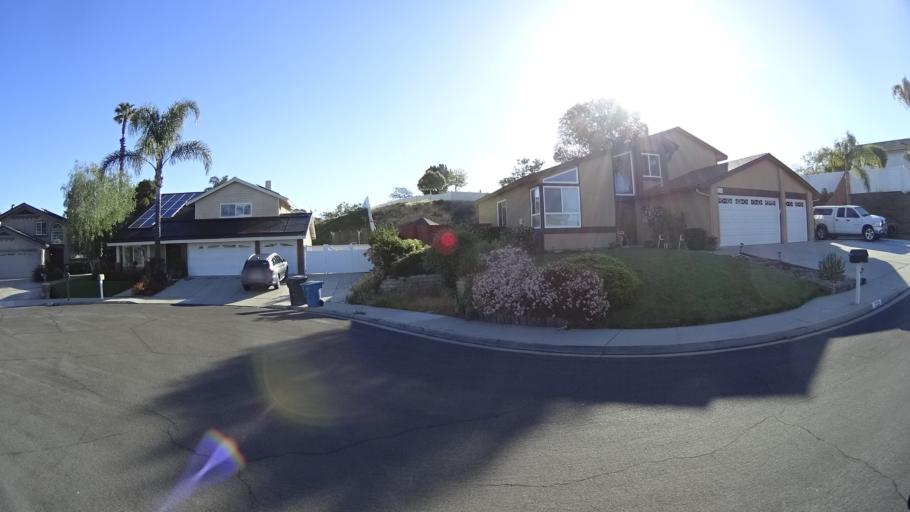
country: US
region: California
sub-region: Ventura County
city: Casa Conejo
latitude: 34.2198
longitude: -118.8957
